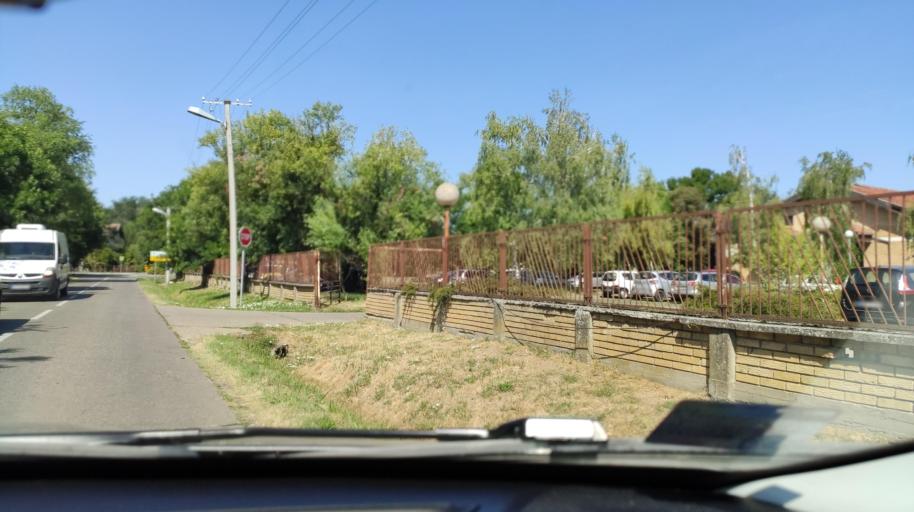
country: RS
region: Autonomna Pokrajina Vojvodina
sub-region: Severnobacki Okrug
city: Backa Topola
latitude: 45.8217
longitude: 19.6326
